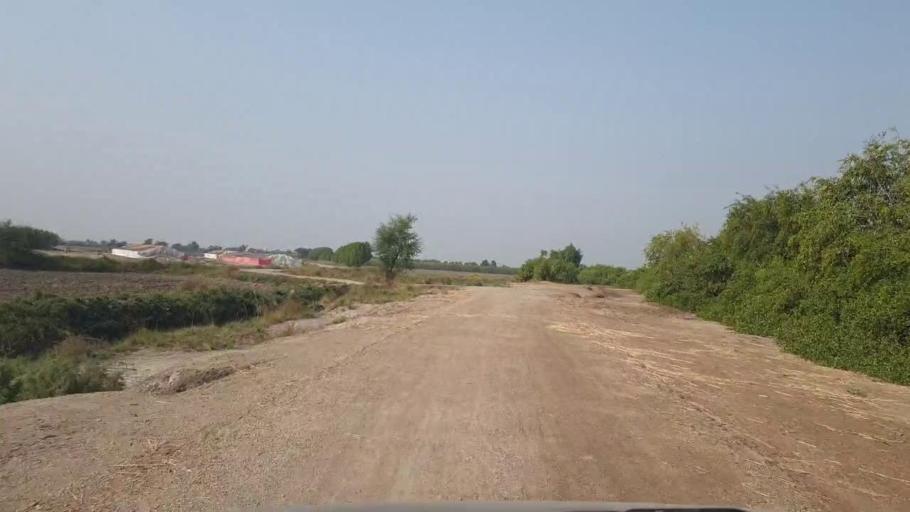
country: PK
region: Sindh
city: Tando Muhammad Khan
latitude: 25.0480
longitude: 68.3725
